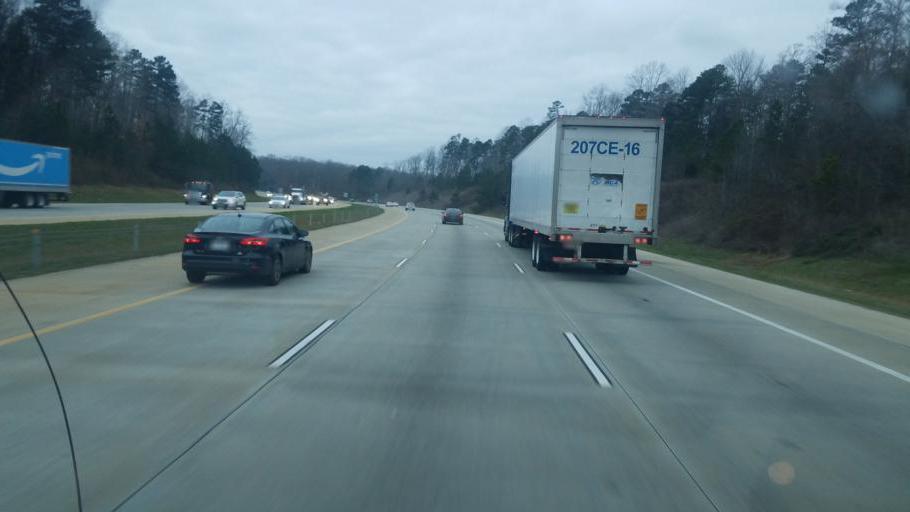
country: US
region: North Carolina
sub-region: Mecklenburg County
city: Huntersville
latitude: 35.3403
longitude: -80.9000
